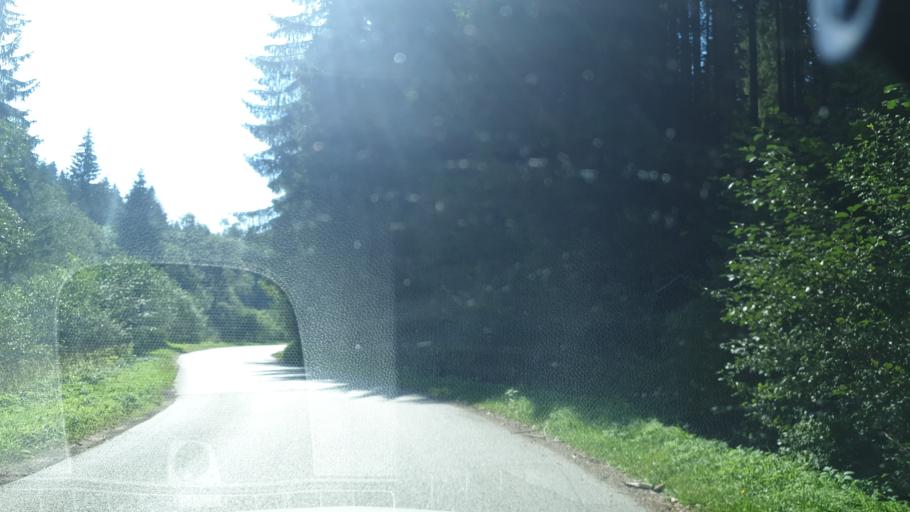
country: RS
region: Central Serbia
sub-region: Zlatiborski Okrug
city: Nova Varos
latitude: 43.4545
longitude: 19.8419
